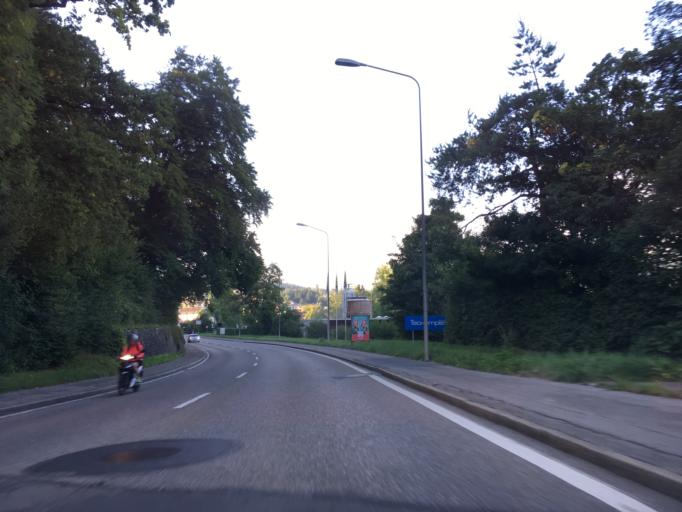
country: CH
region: Zurich
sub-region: Bezirk Horgen
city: Adliswil / Sood
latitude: 47.3189
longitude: 8.5291
